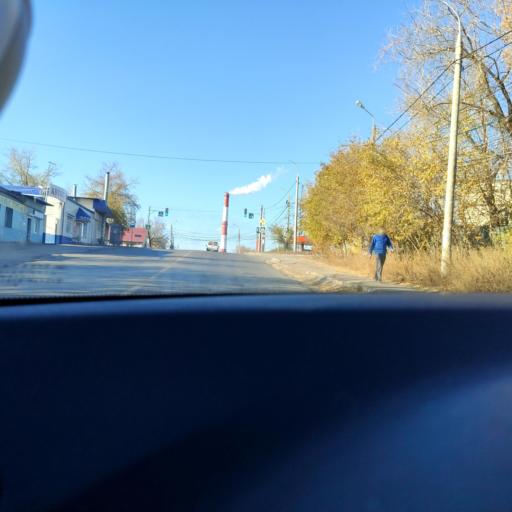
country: RU
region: Samara
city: Samara
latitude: 53.1823
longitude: 50.1640
